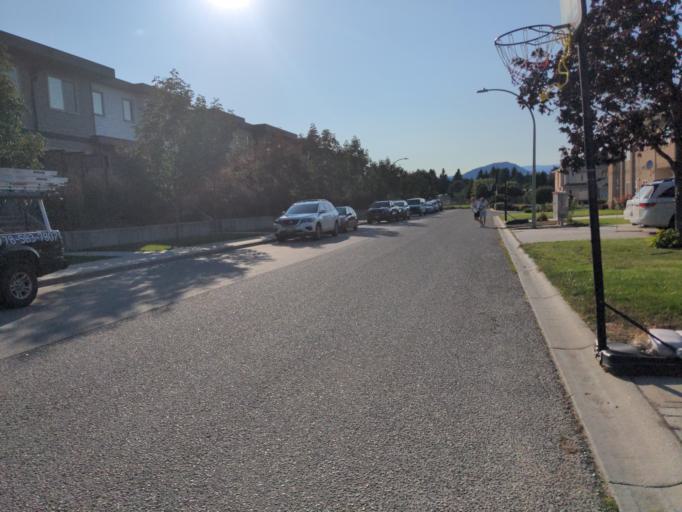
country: CA
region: British Columbia
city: Kelowna
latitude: 49.8541
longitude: -119.4776
